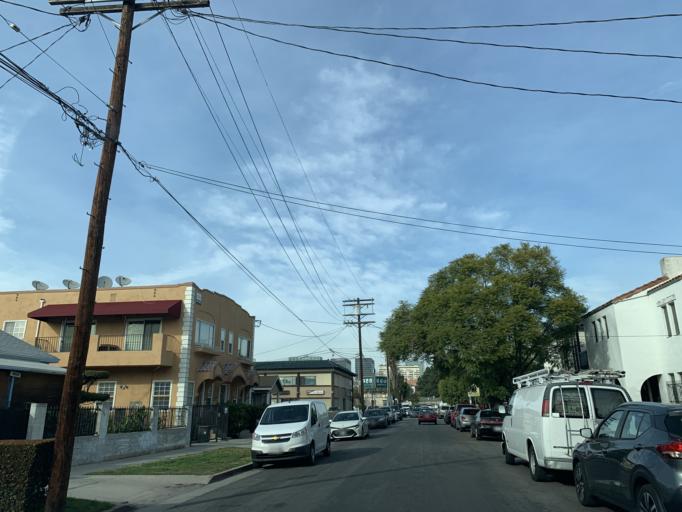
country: US
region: California
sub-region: Los Angeles County
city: Silver Lake
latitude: 34.0514
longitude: -118.3010
